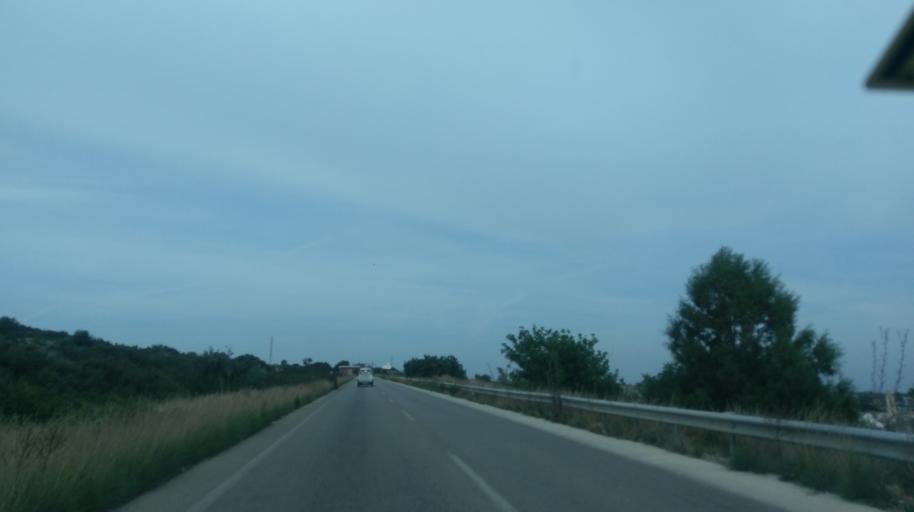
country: CY
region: Ammochostos
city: Leonarisso
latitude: 35.4266
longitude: 34.1272
